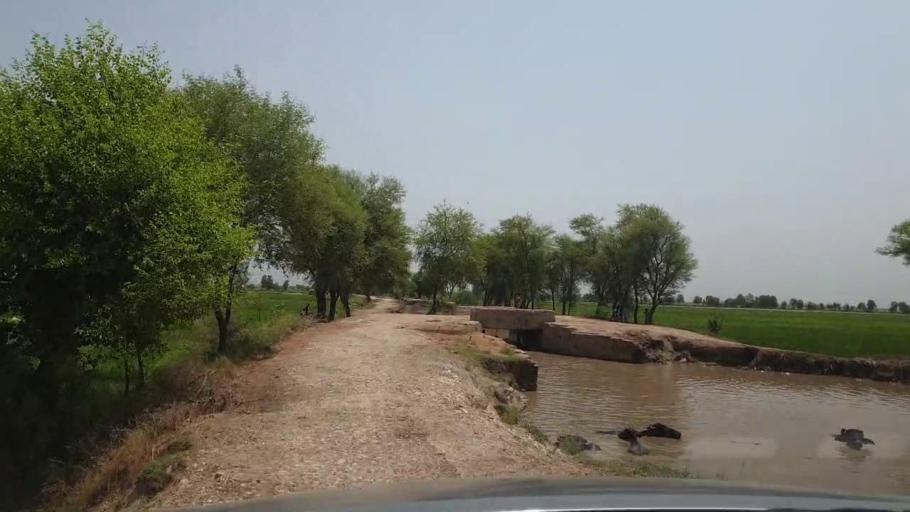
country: PK
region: Sindh
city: Madeji
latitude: 27.7777
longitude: 68.4023
